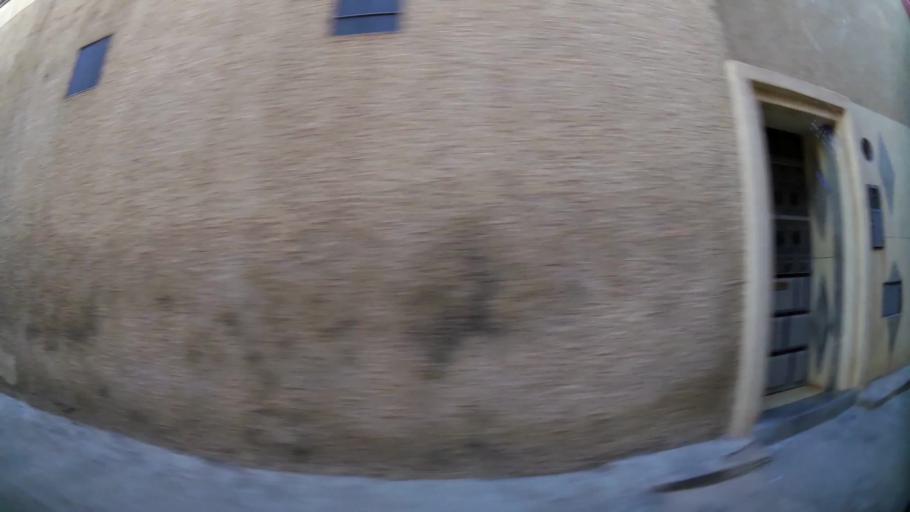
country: MA
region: Oriental
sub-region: Oujda-Angad
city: Oujda
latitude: 34.6795
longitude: -1.8884
